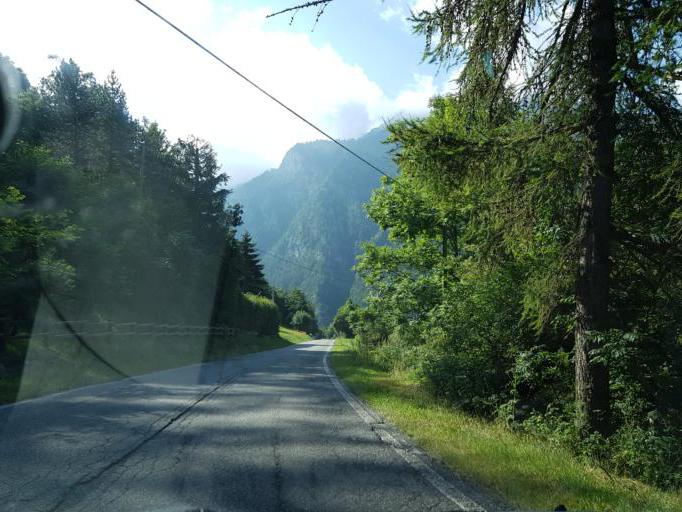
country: IT
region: Piedmont
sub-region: Provincia di Cuneo
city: Casteldelfino
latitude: 44.5933
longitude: 7.0700
